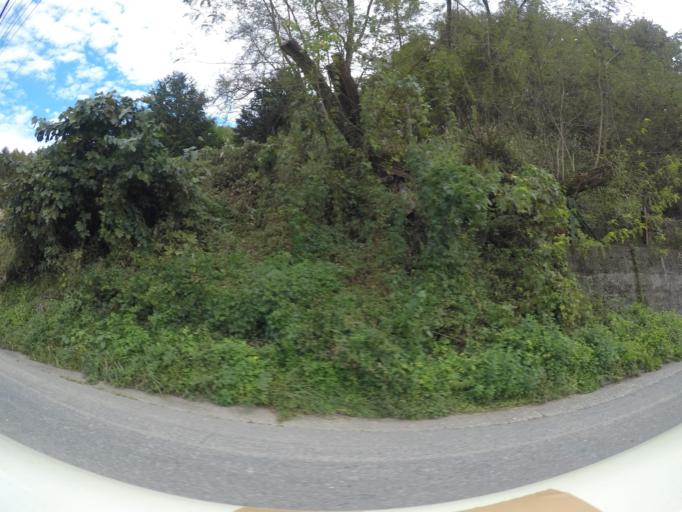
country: JP
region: Nagano
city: Chino
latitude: 35.9124
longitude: 138.0941
